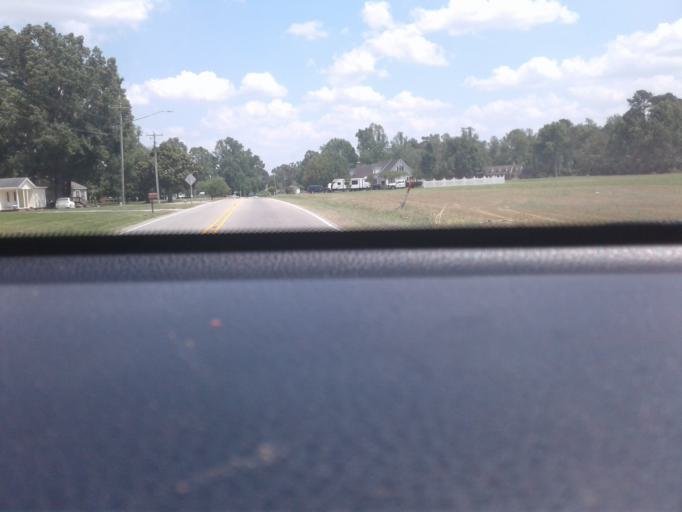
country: US
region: North Carolina
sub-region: Harnett County
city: Erwin
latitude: 35.3110
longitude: -78.6755
